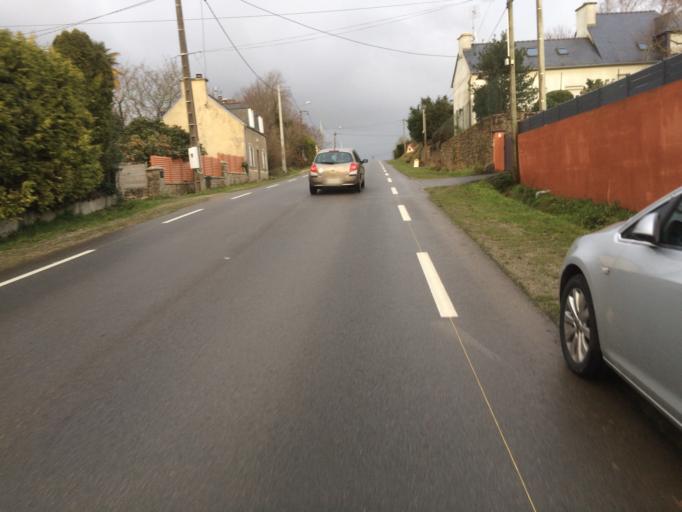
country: FR
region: Brittany
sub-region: Departement du Finistere
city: Logonna-Daoulas
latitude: 48.3311
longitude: -4.2919
